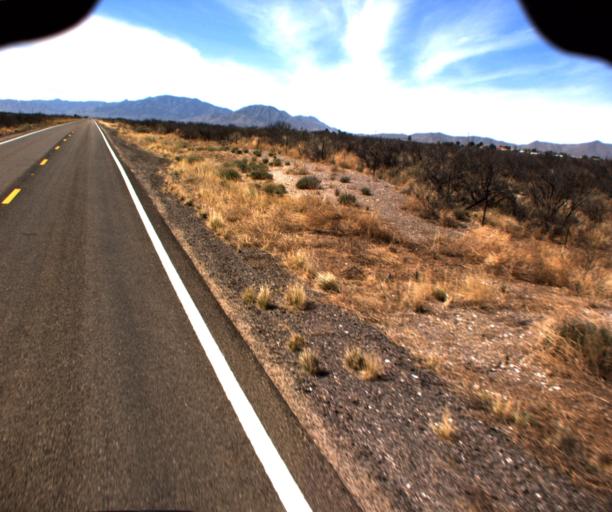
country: US
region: Arizona
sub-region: Cochise County
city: Willcox
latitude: 32.1187
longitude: -109.9110
